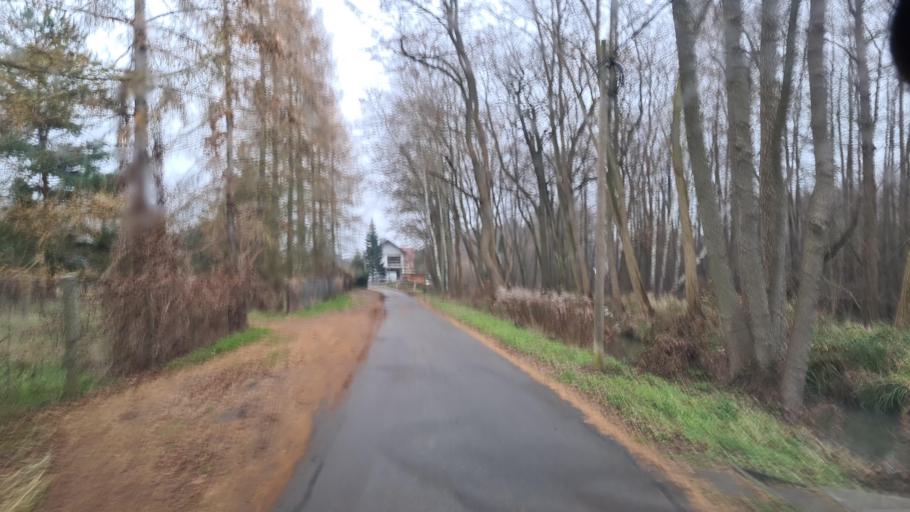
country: DE
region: Brandenburg
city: Kolkwitz
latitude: 51.7477
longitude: 14.2740
